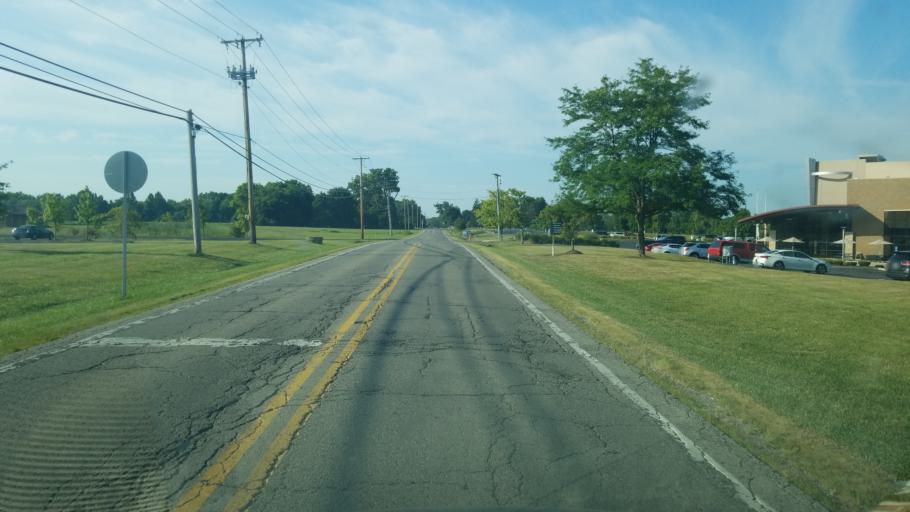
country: US
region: Ohio
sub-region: Franklin County
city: Lincoln Village
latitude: 39.9591
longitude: -83.1670
